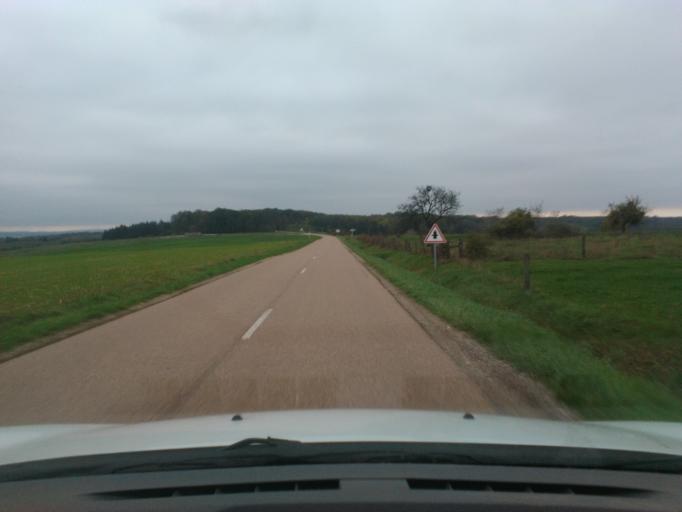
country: FR
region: Lorraine
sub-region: Departement des Vosges
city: Charmes
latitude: 48.3028
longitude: 6.2475
